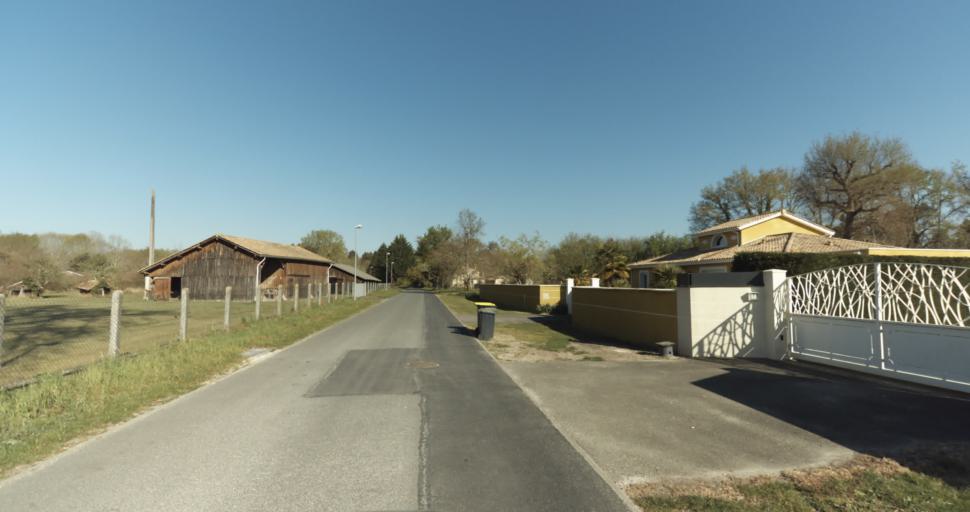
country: FR
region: Aquitaine
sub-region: Departement de la Gironde
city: Martignas-sur-Jalle
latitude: 44.8035
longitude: -0.8406
